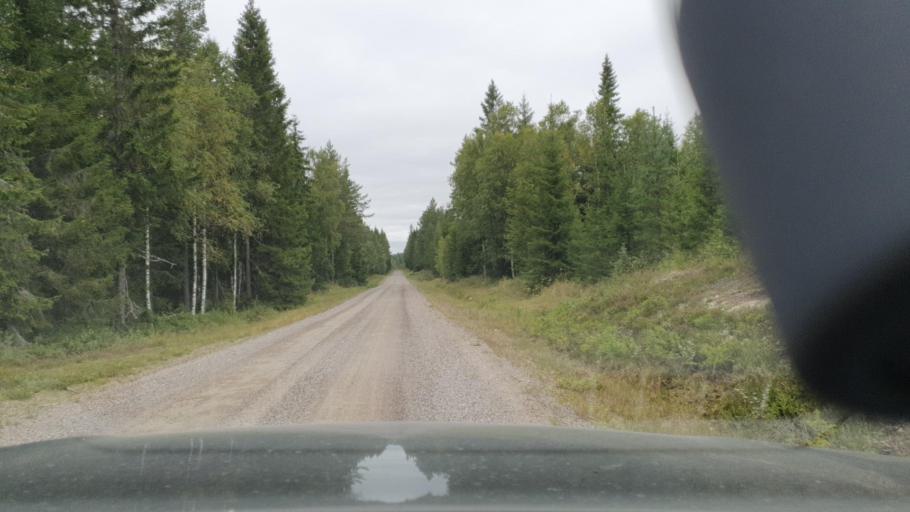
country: SE
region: Vaermland
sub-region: Eda Kommun
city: Charlottenberg
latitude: 60.1169
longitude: 12.6026
